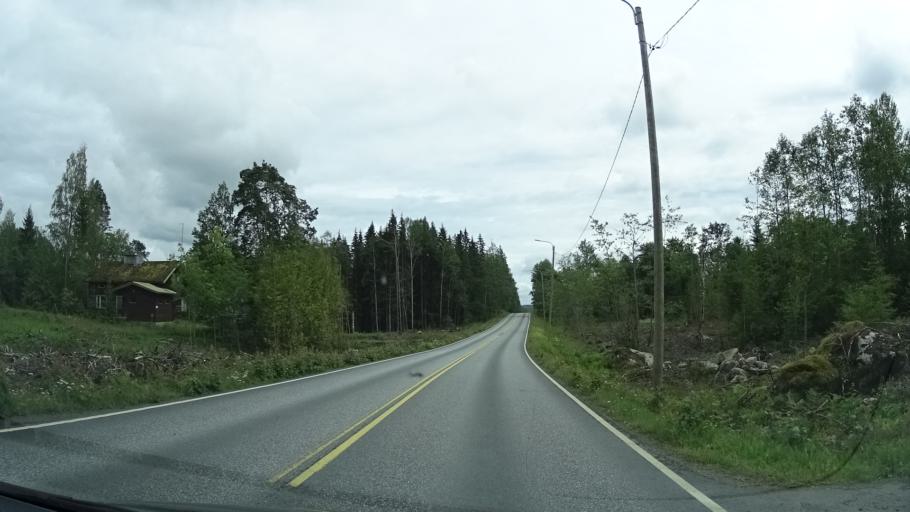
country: FI
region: Pirkanmaa
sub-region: Etelae-Pirkanmaa
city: Urjala
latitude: 61.0846
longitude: 23.4212
